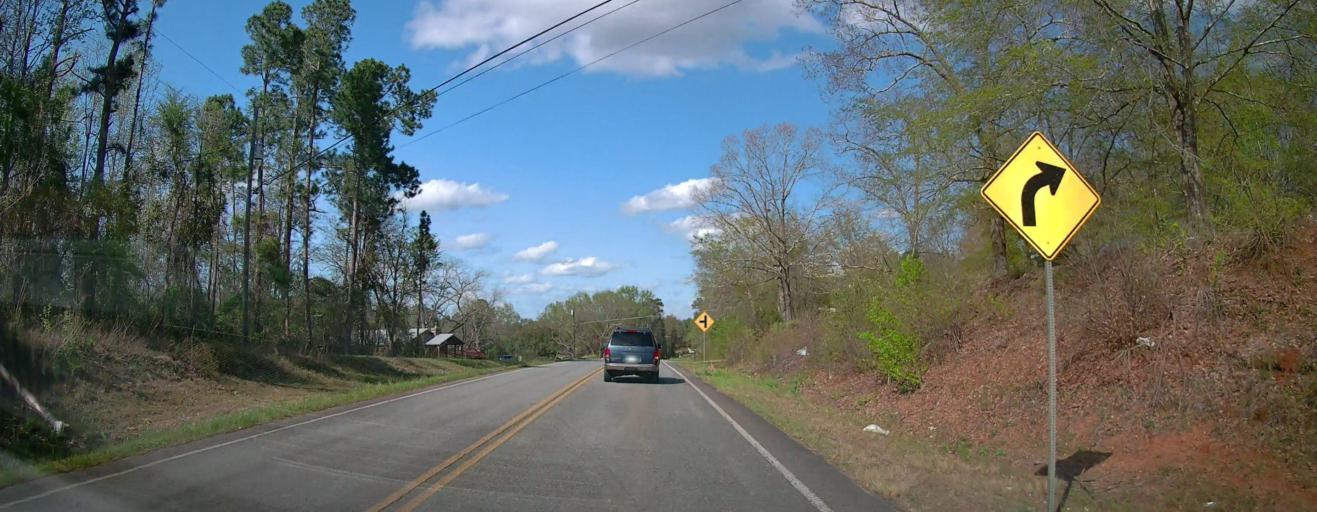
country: US
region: Georgia
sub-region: Baldwin County
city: Hardwick
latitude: 33.0003
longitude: -83.2566
